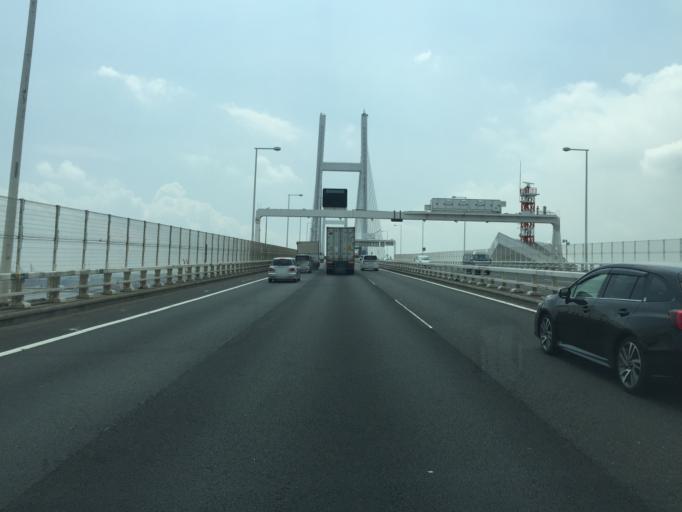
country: JP
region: Kanagawa
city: Yokohama
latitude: 35.4601
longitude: 139.6777
